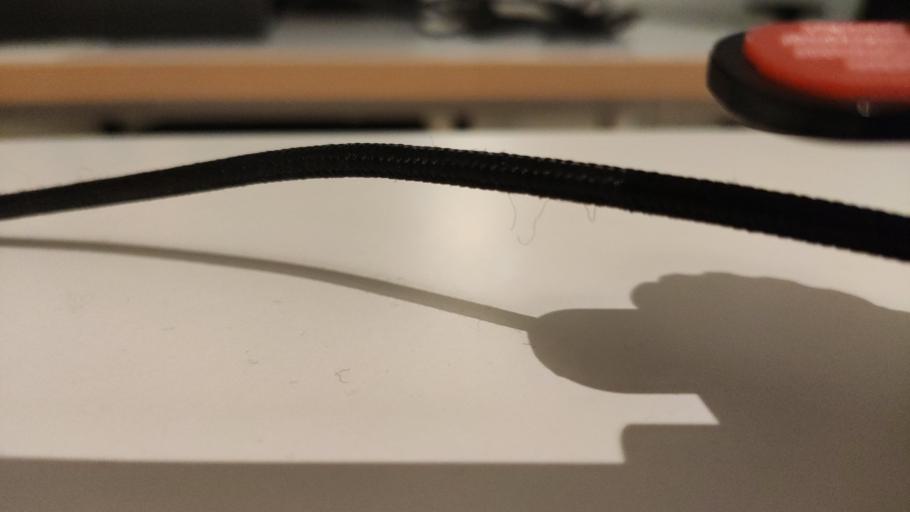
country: RU
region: Moskovskaya
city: Novosin'kovo
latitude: 56.3809
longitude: 37.3237
